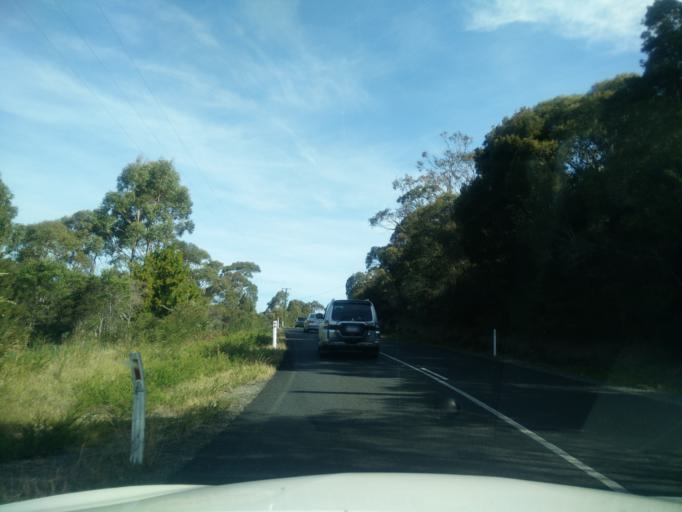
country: AU
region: Tasmania
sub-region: Break O'Day
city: St Helens
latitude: -41.2951
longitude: 148.2739
